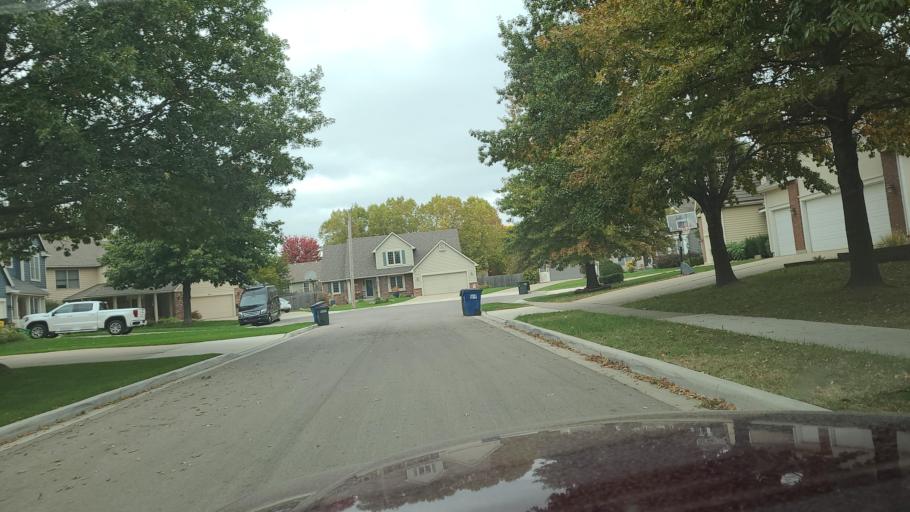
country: US
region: Kansas
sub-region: Douglas County
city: Lawrence
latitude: 38.9683
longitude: -95.3124
